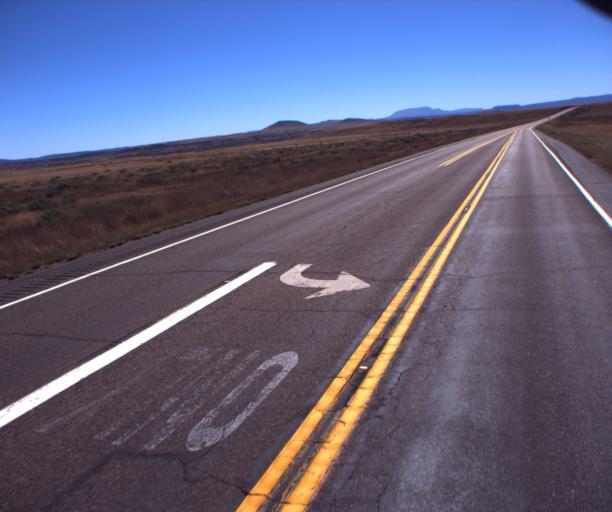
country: US
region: Arizona
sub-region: Apache County
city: Saint Johns
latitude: 34.3225
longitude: -109.3841
